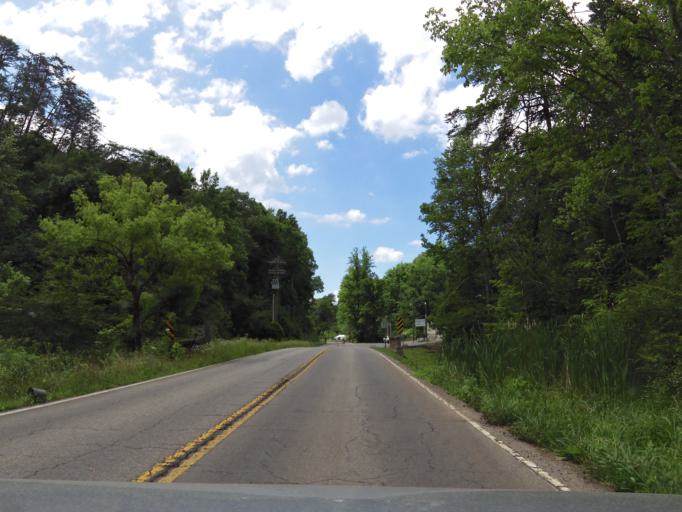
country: US
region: Tennessee
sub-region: Loudon County
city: Greenback
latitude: 35.5700
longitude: -84.0950
